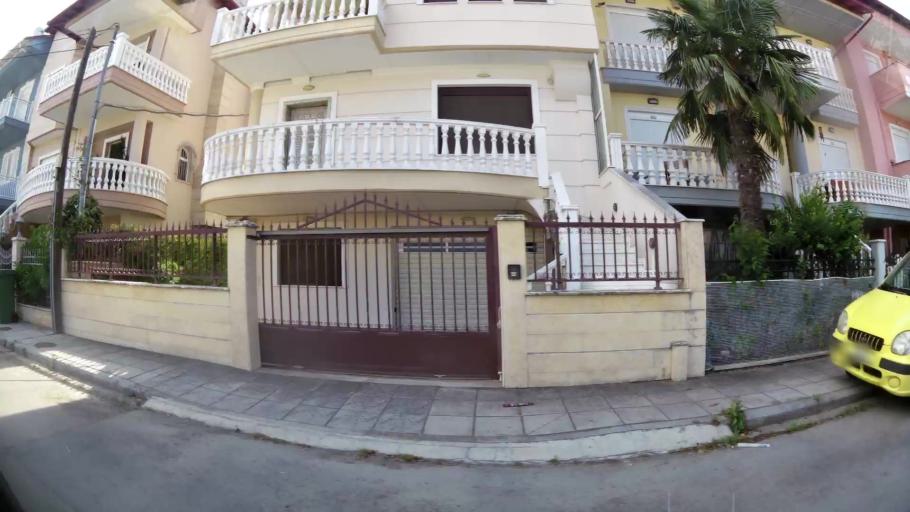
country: GR
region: Central Macedonia
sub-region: Nomos Pierias
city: Katerini
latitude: 40.2845
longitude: 22.5093
